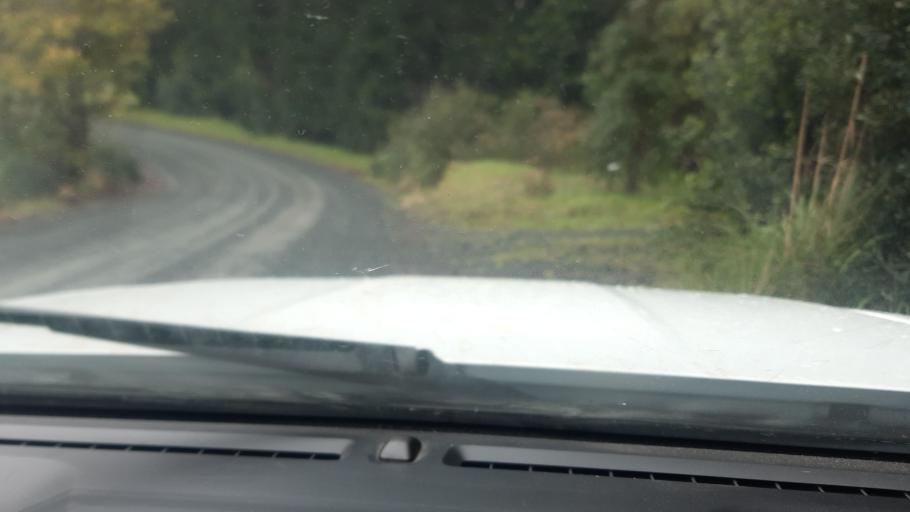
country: NZ
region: Northland
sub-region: Far North District
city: Kaitaia
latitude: -34.9793
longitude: 173.2027
